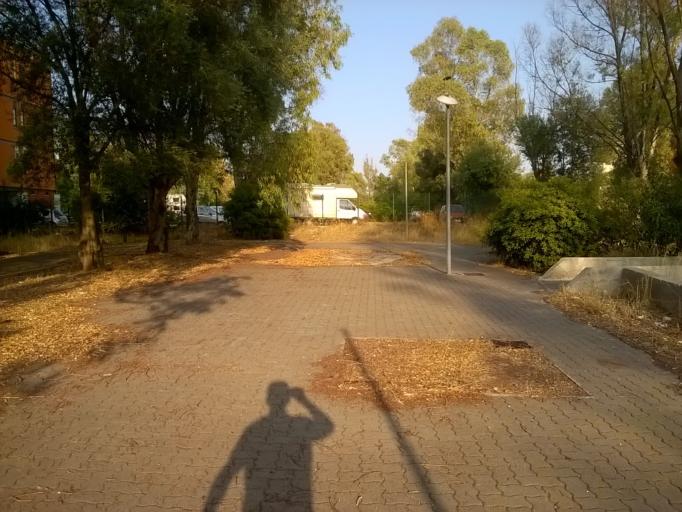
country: IT
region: Apulia
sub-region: Provincia di Taranto
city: Paolo VI
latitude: 40.5198
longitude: 17.2779
